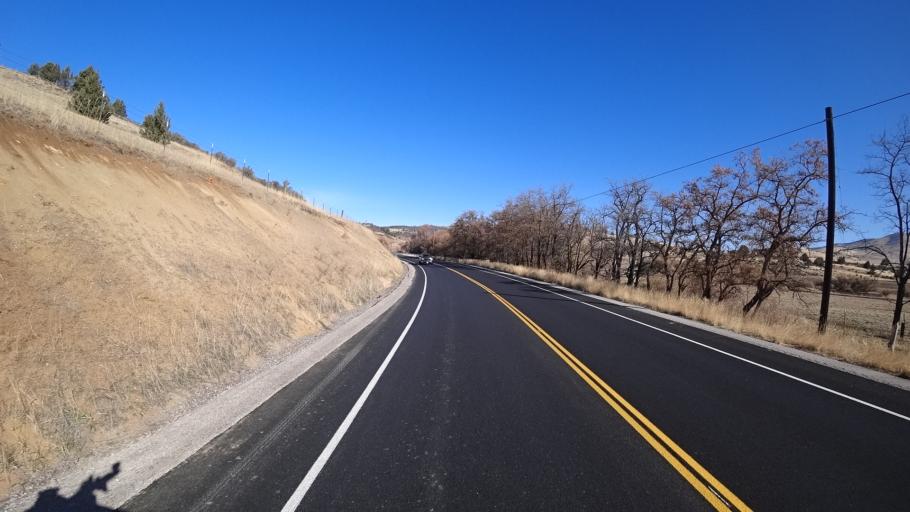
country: US
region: California
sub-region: Siskiyou County
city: Montague
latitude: 41.8527
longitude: -122.4653
